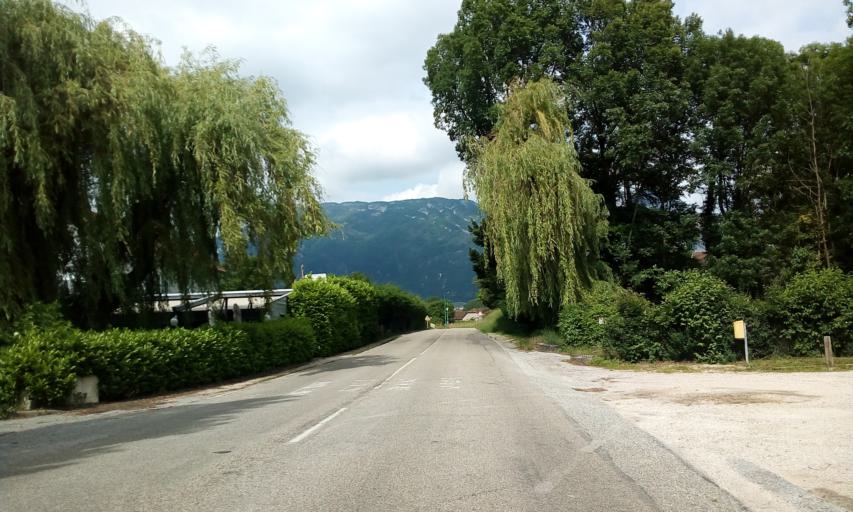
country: FR
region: Rhone-Alpes
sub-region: Departement de la Savoie
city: Les Marches
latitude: 45.4940
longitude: 5.9890
